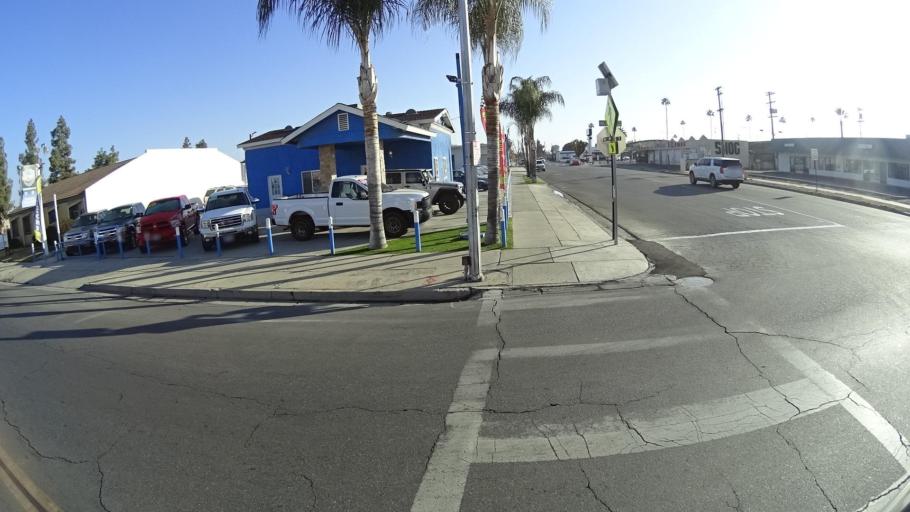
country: US
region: California
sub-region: Kern County
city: Delano
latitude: 35.7677
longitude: -119.2467
